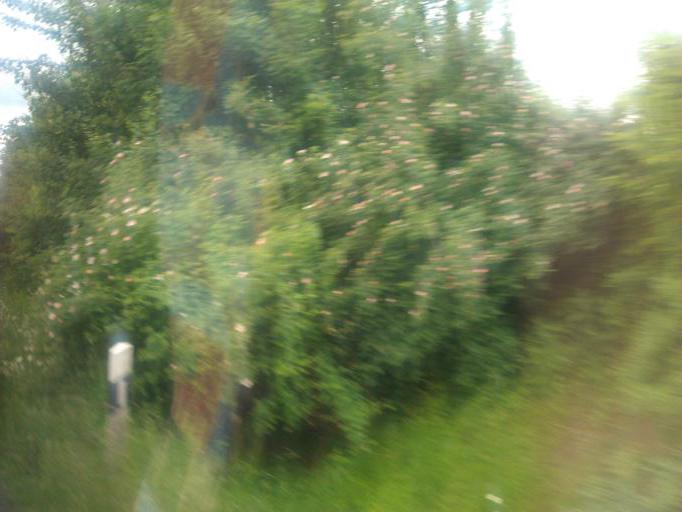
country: DE
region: North Rhine-Westphalia
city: Julich
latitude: 50.9101
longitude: 6.3269
